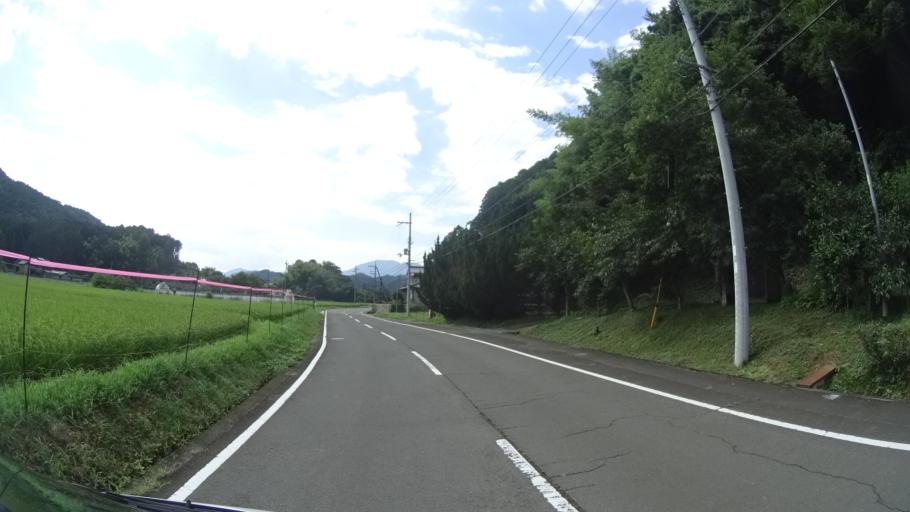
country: JP
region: Kyoto
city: Fukuchiyama
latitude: 35.3750
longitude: 135.1483
